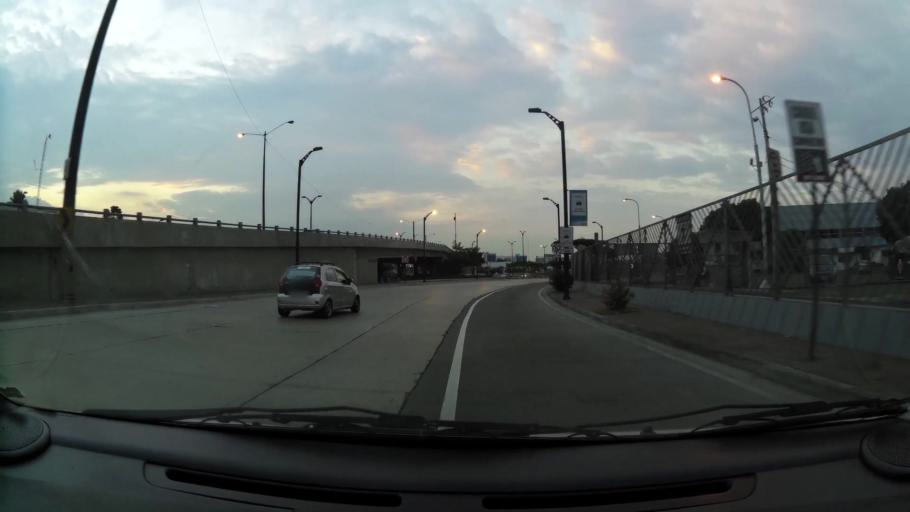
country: EC
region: Guayas
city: Eloy Alfaro
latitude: -2.1652
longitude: -79.8919
